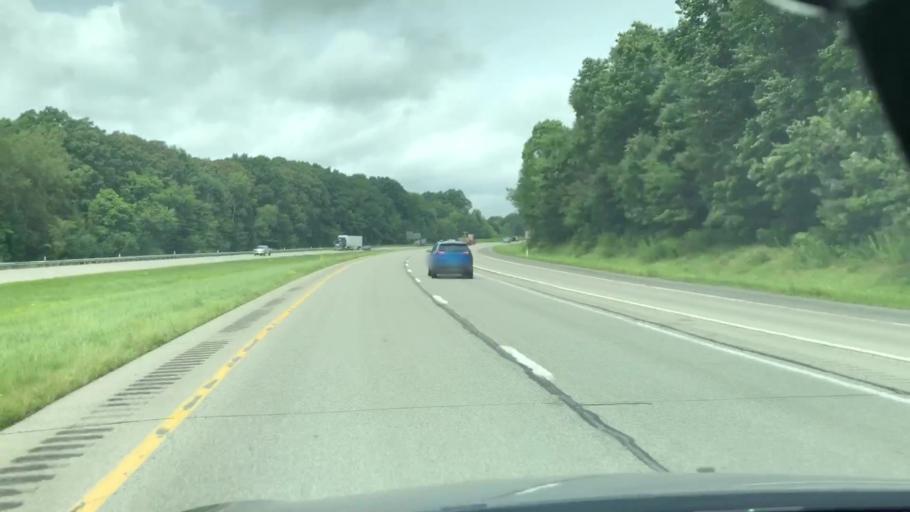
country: US
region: Pennsylvania
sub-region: Butler County
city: Slippery Rock
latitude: 41.0403
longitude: -80.1267
